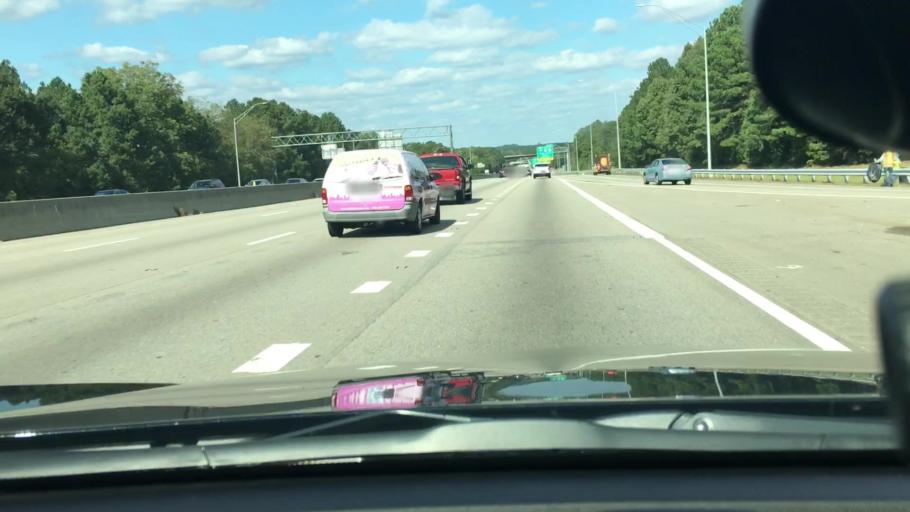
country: US
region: North Carolina
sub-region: Wake County
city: Raleigh
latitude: 35.7704
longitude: -78.5739
